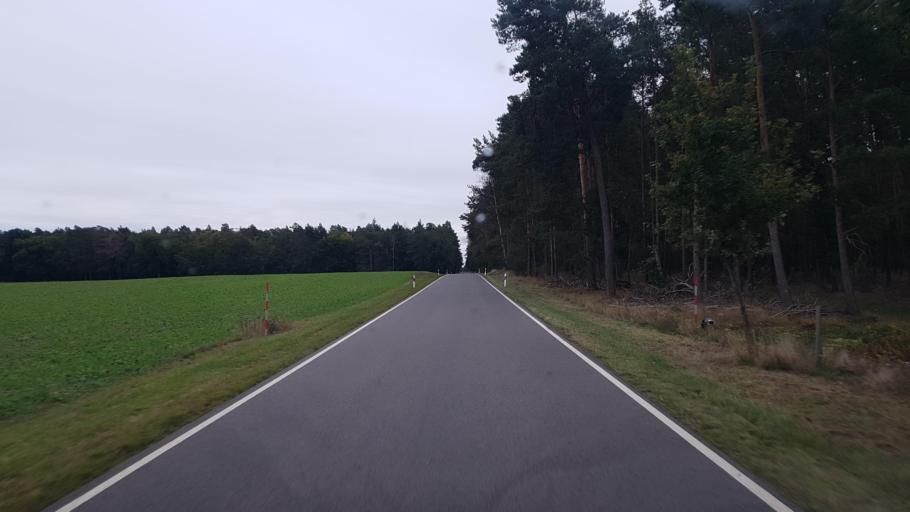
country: DE
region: Brandenburg
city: Luckau
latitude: 51.8873
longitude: 13.6628
